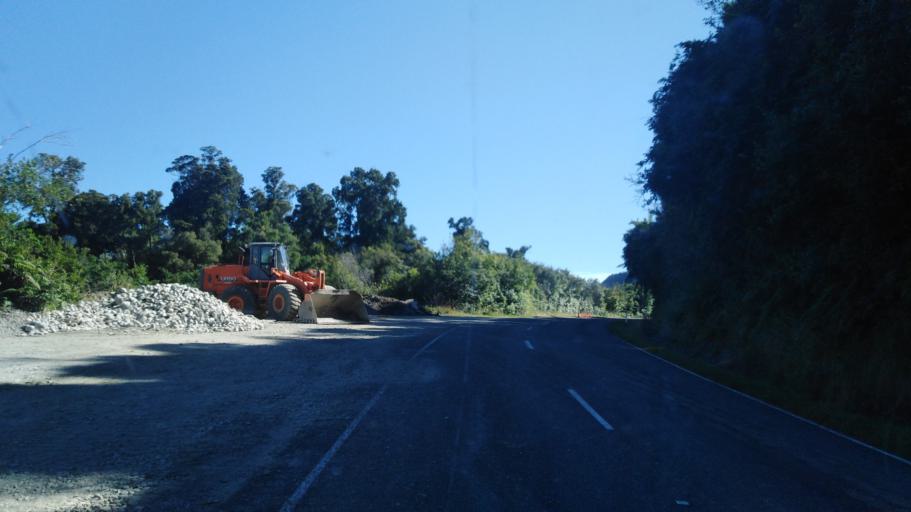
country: NZ
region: West Coast
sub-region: Buller District
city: Westport
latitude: -41.5278
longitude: 172.0088
